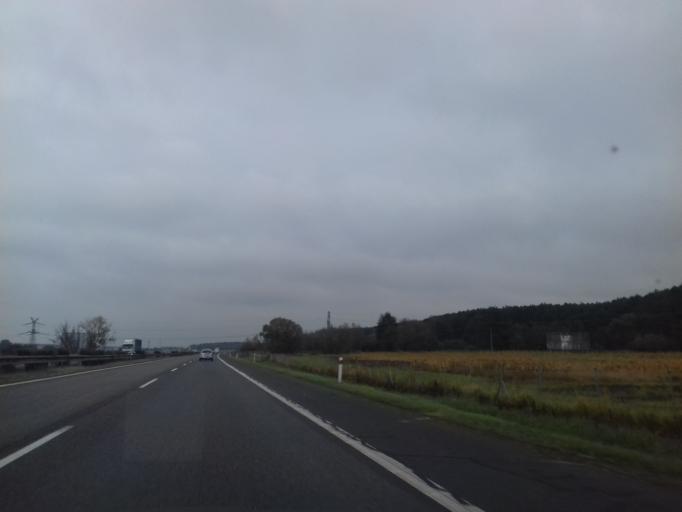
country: SK
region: Bratislavsky
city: Stupava
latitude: 48.3065
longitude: 17.0167
